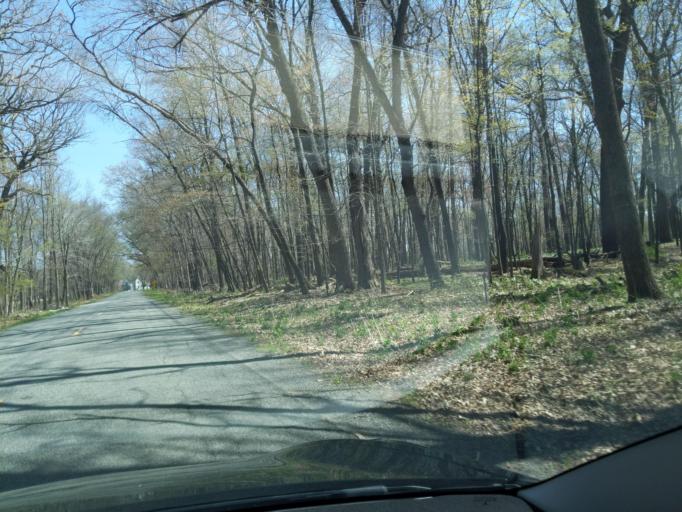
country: US
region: Michigan
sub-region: Ingham County
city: Stockbridge
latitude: 42.4847
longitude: -84.1704
